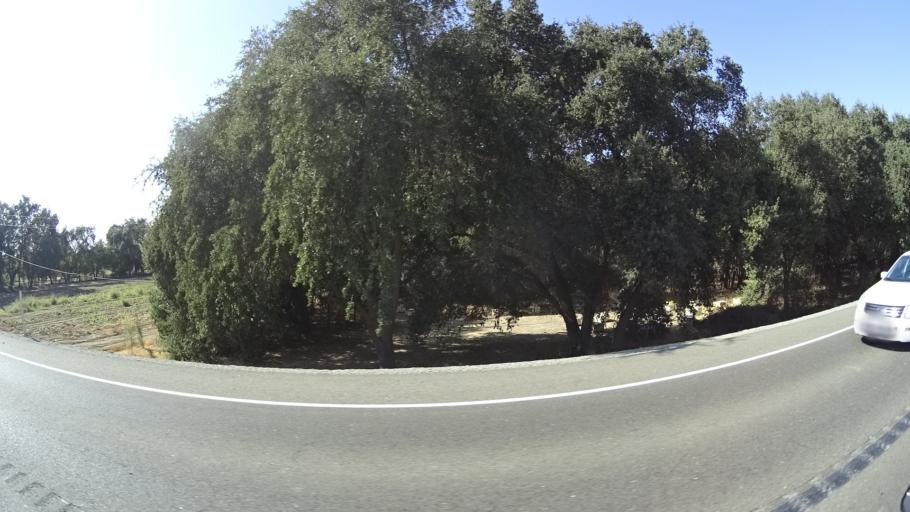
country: US
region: California
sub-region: Yolo County
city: West Sacramento
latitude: 38.6351
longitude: -121.5646
